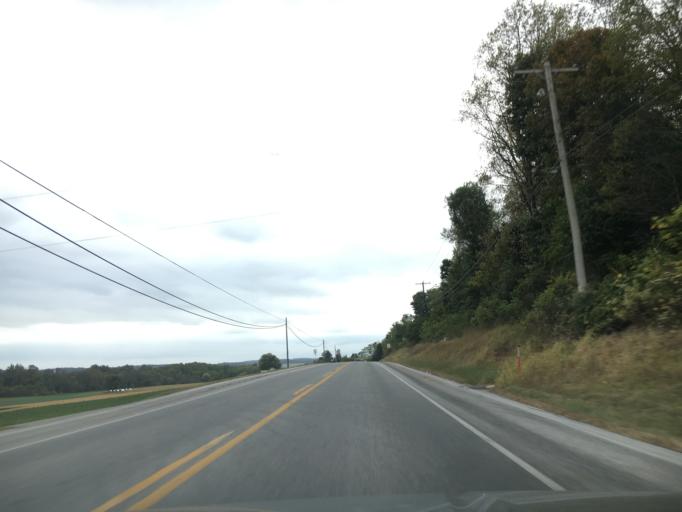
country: US
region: Pennsylvania
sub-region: Lancaster County
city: Quarryville
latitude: 39.9048
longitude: -76.1370
